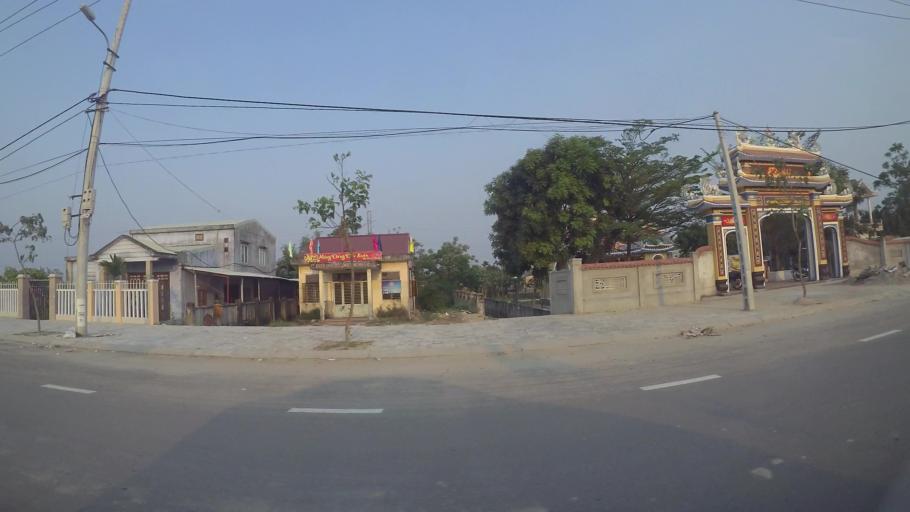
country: VN
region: Da Nang
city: Ngu Hanh Son
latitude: 15.9640
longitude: 108.2313
